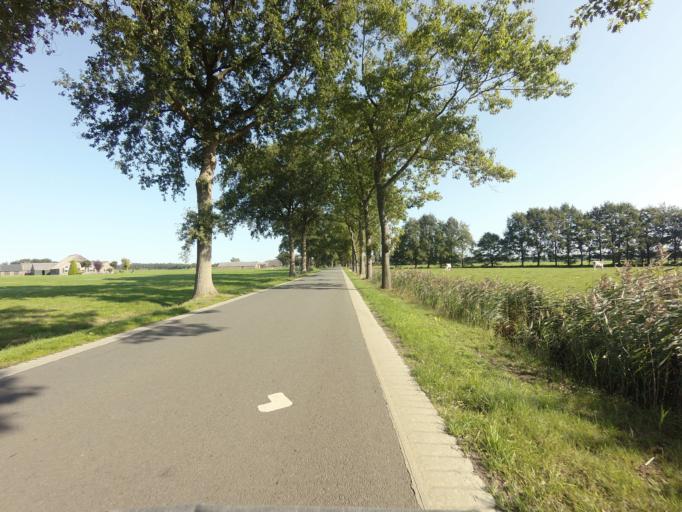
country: NL
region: Overijssel
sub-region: Gemeente Raalte
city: Raalte
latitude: 52.4115
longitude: 6.2860
